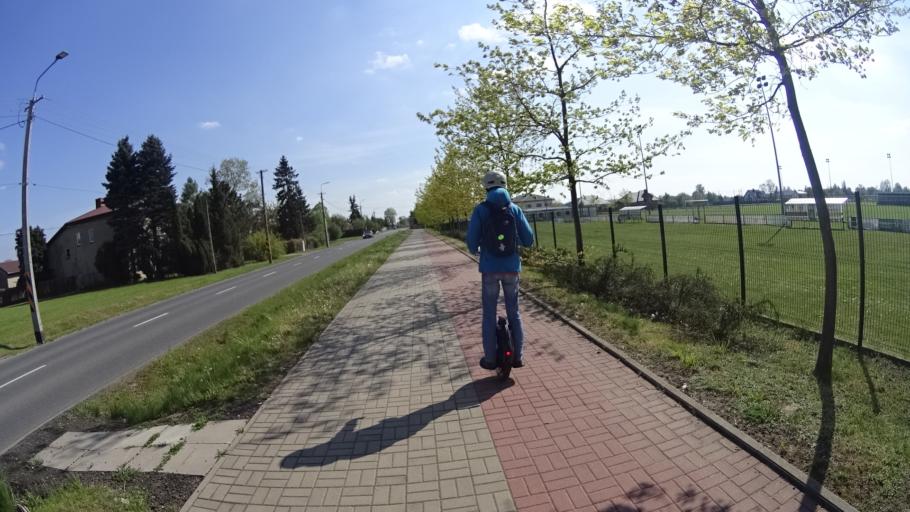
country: PL
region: Masovian Voivodeship
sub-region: Powiat warszawski zachodni
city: Stare Babice
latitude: 52.2448
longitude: 20.8190
